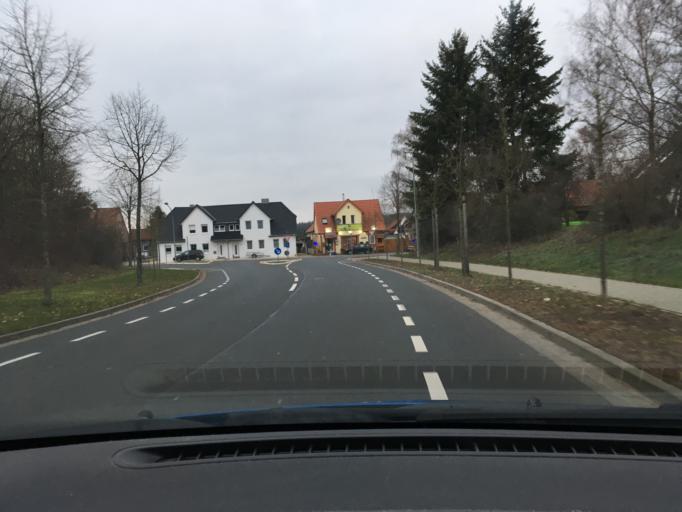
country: DE
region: Lower Saxony
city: Walsrode
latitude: 52.8569
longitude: 9.5783
